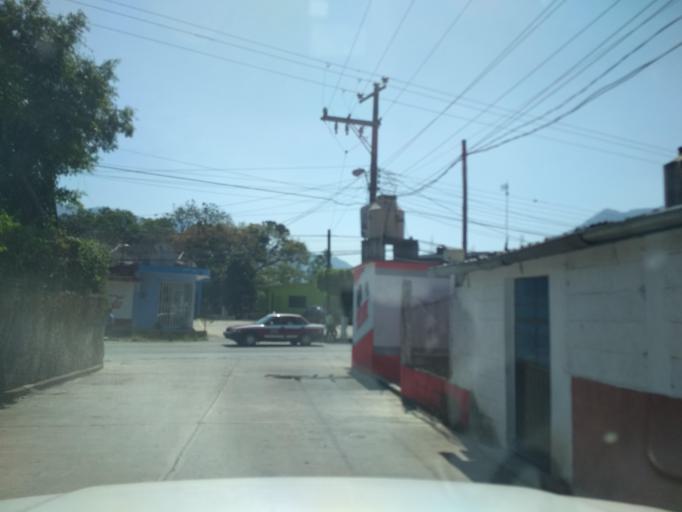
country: MX
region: Veracruz
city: Jalapilla
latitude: 18.8200
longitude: -97.0898
